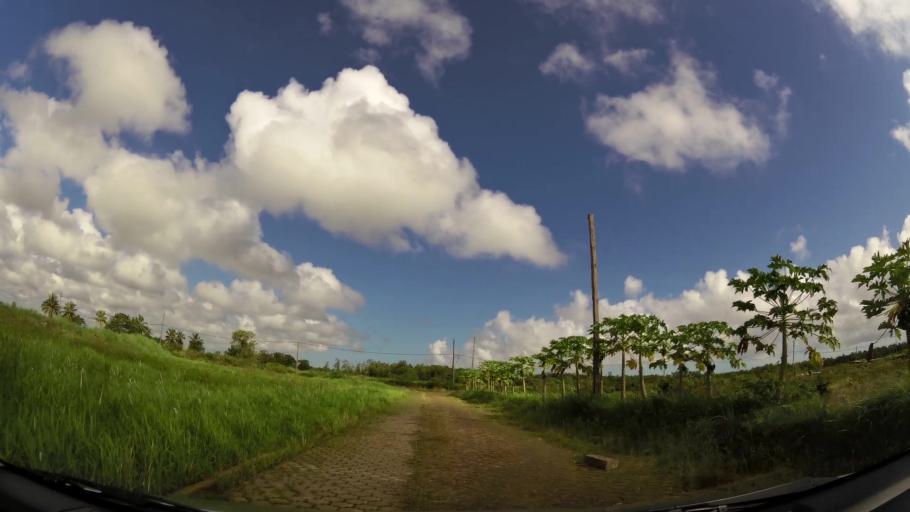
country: SR
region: Commewijne
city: Nieuw Amsterdam
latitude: 5.8805
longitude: -55.1158
